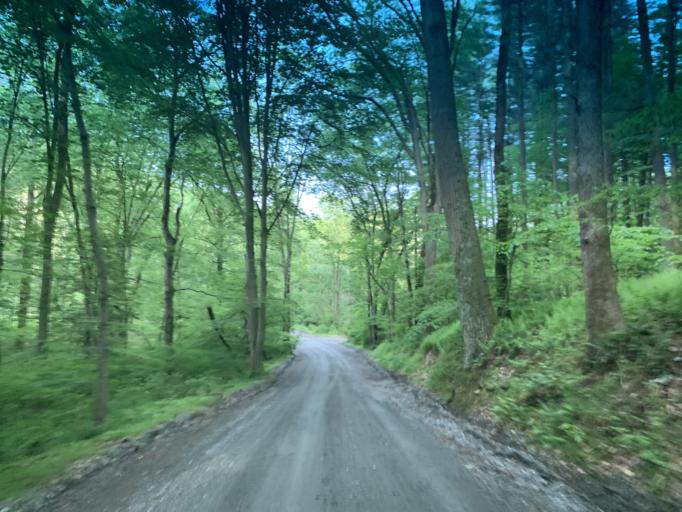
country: US
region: Pennsylvania
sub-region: York County
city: Susquehanna Trails
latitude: 39.6989
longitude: -76.2646
